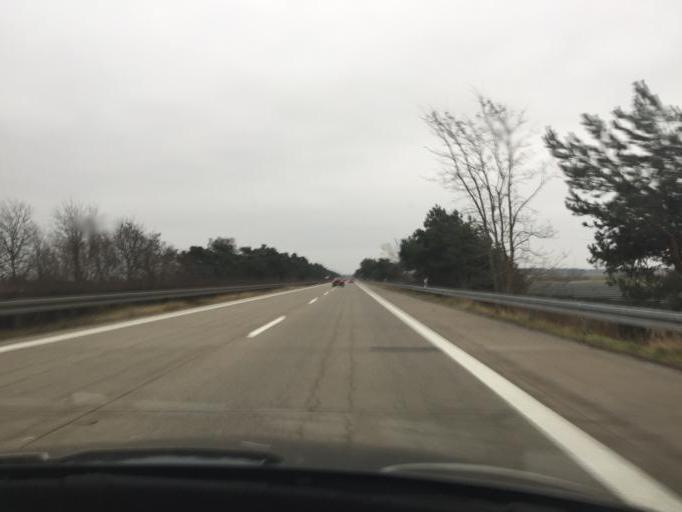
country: DE
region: Brandenburg
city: Vetschau
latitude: 51.8108
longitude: 14.0285
